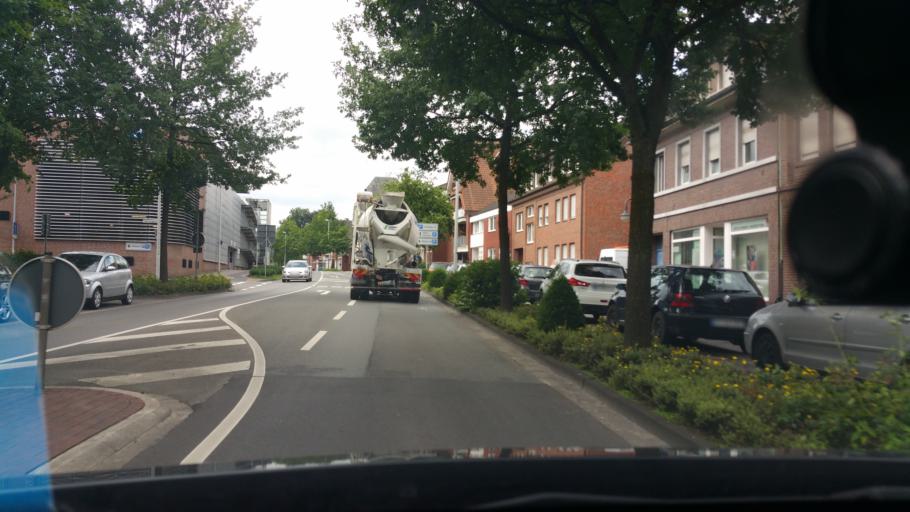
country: DE
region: North Rhine-Westphalia
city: Emsdetten
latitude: 52.1755
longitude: 7.5266
